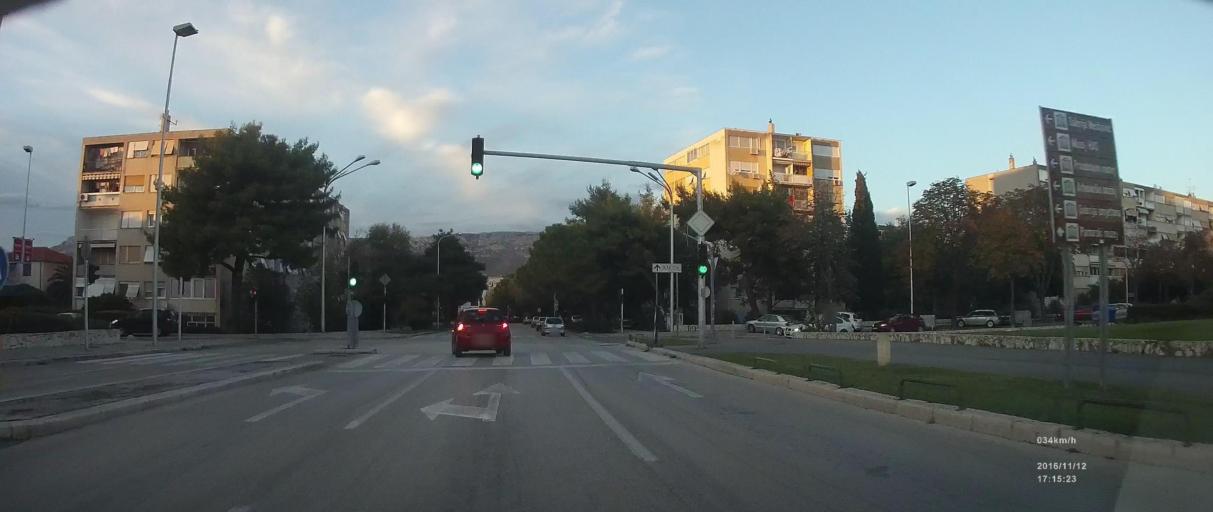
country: HR
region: Splitsko-Dalmatinska
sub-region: Grad Split
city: Split
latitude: 43.5128
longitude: 16.4492
